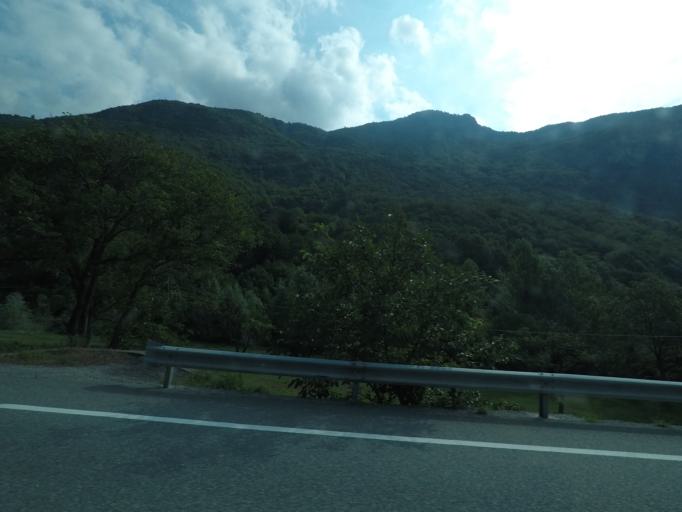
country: IT
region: Aosta Valley
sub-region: Valle d'Aosta
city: Chatillon
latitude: 45.7665
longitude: 7.6033
